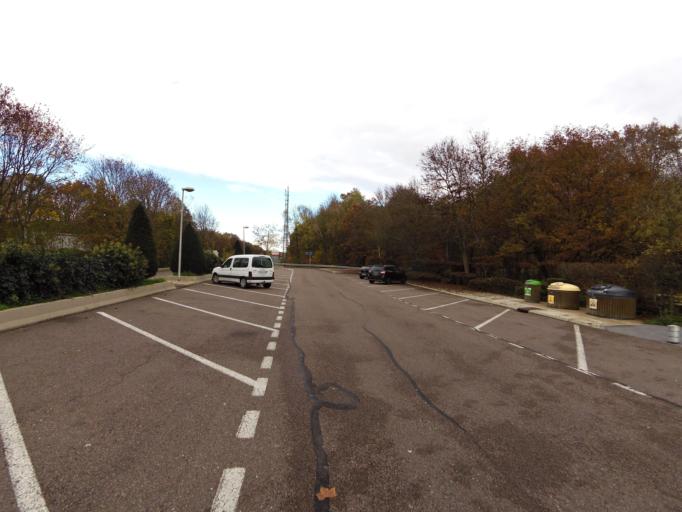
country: FR
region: Bourgogne
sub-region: Departement de Saone-et-Loire
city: Champforgeuil
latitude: 46.8612
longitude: 4.8232
